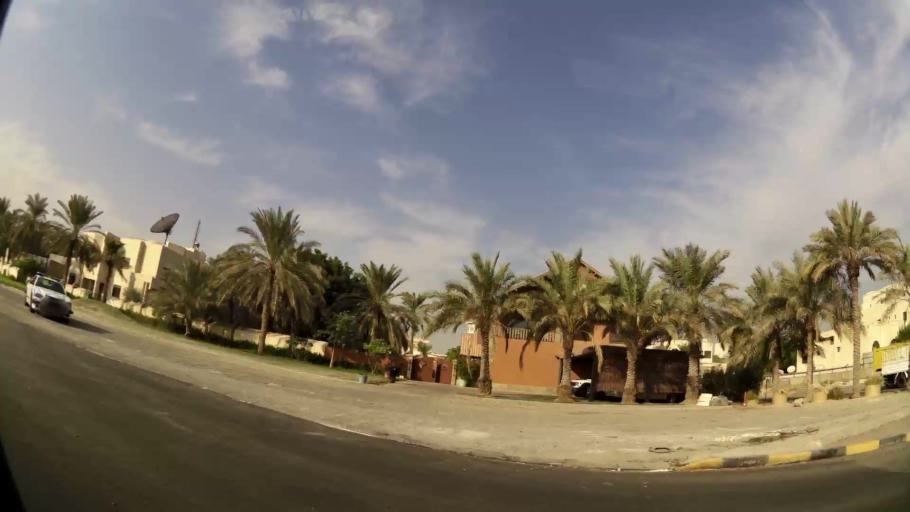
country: KW
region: Muhafazat Hawalli
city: Salwa
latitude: 29.2885
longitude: 48.0859
